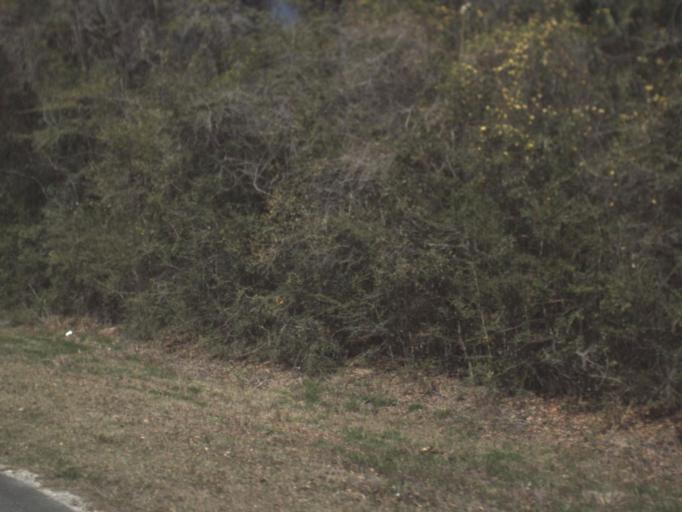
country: US
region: Florida
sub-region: Leon County
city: Woodville
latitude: 30.2361
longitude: -84.2479
